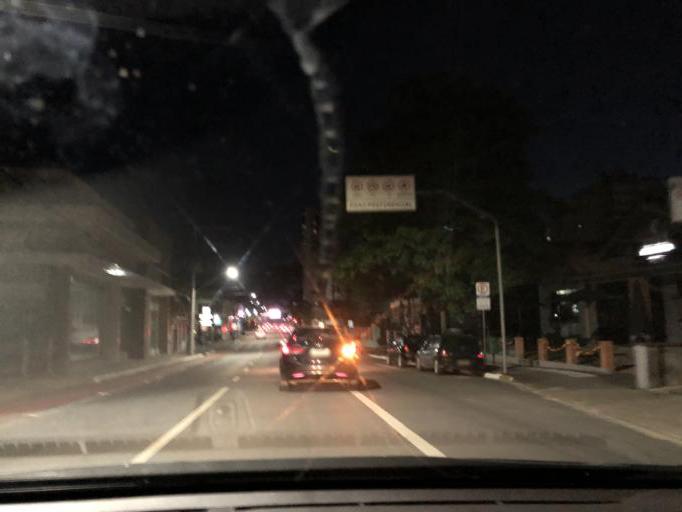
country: BR
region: Santa Catarina
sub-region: Jaragua Do Sul
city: Jaragua do Sul
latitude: -26.4817
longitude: -49.0843
